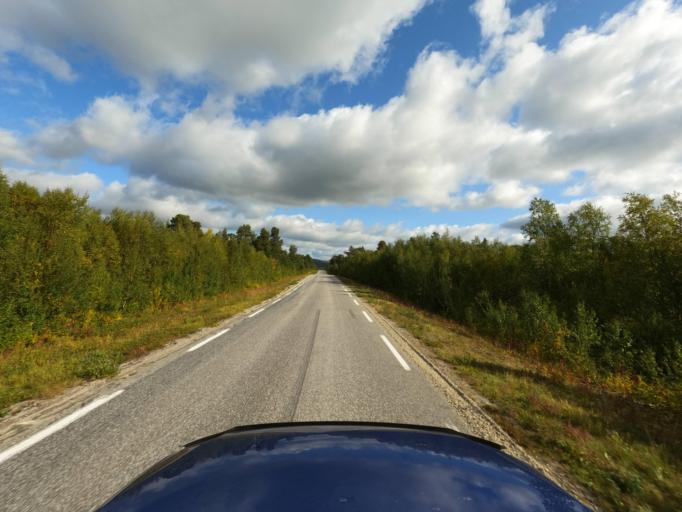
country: NO
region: Finnmark Fylke
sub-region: Karasjok
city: Karasjohka
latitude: 69.4320
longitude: 24.9692
